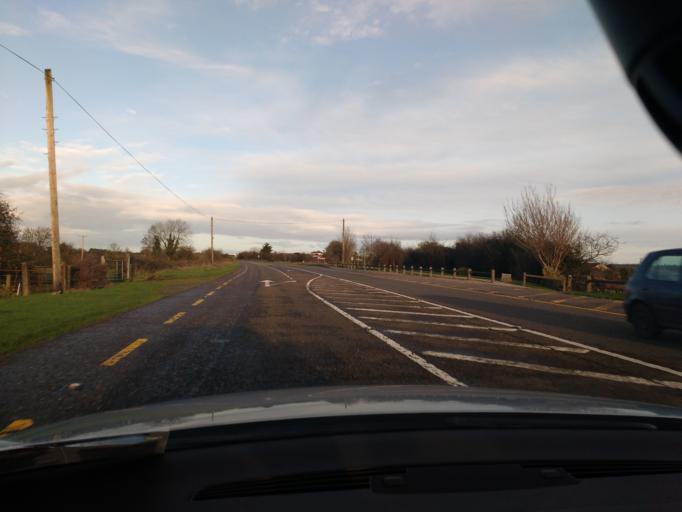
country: IE
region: Munster
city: Thurles
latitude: 52.6753
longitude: -7.6739
